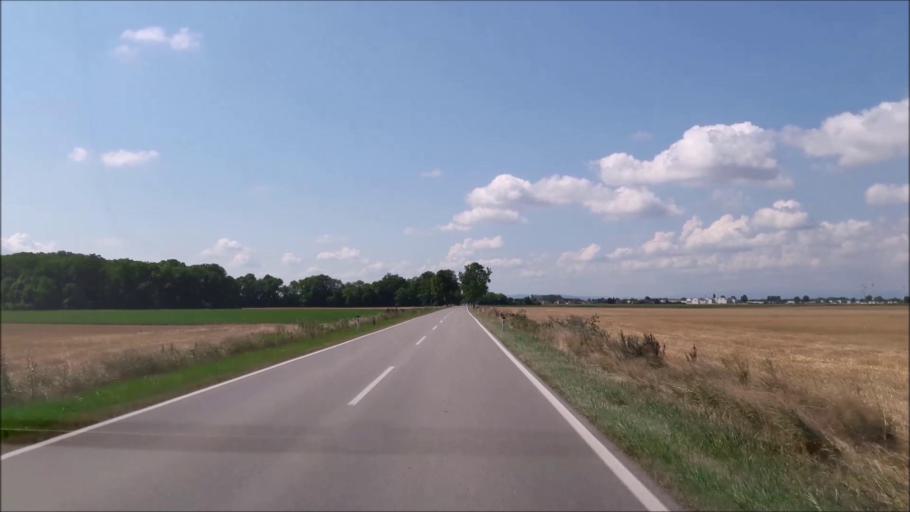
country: AT
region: Lower Austria
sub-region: Politischer Bezirk Baden
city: Mitterndorf an der Fischa
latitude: 47.9780
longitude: 16.4351
